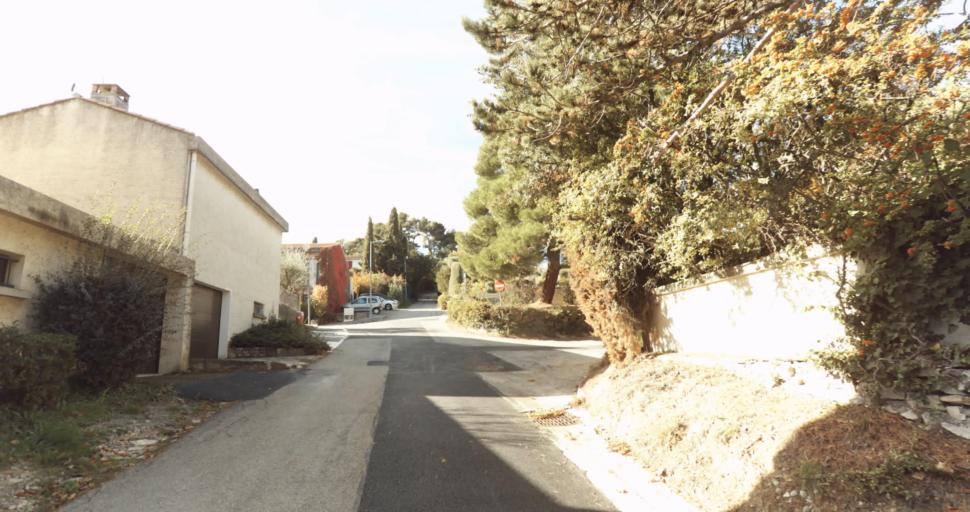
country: FR
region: Provence-Alpes-Cote d'Azur
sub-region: Departement des Bouches-du-Rhone
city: Venelles
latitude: 43.6008
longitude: 5.4830
